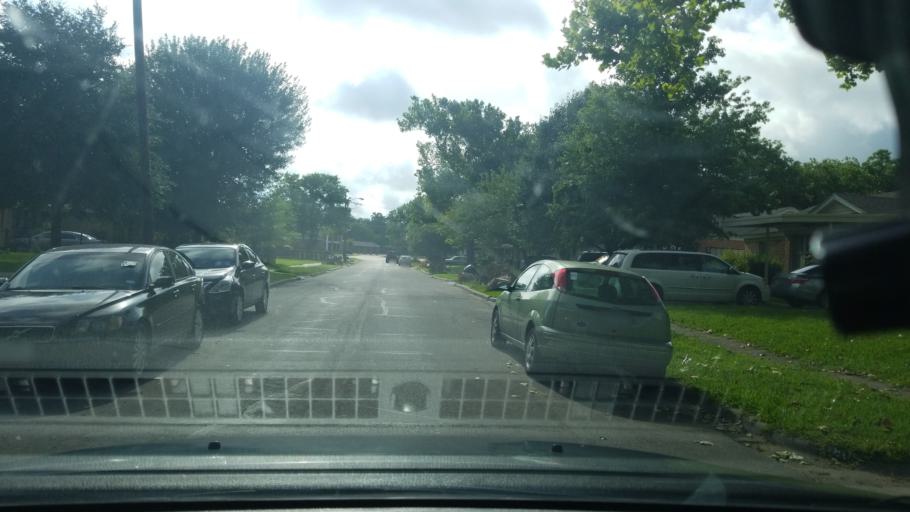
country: US
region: Texas
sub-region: Dallas County
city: Mesquite
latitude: 32.8198
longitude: -96.6670
